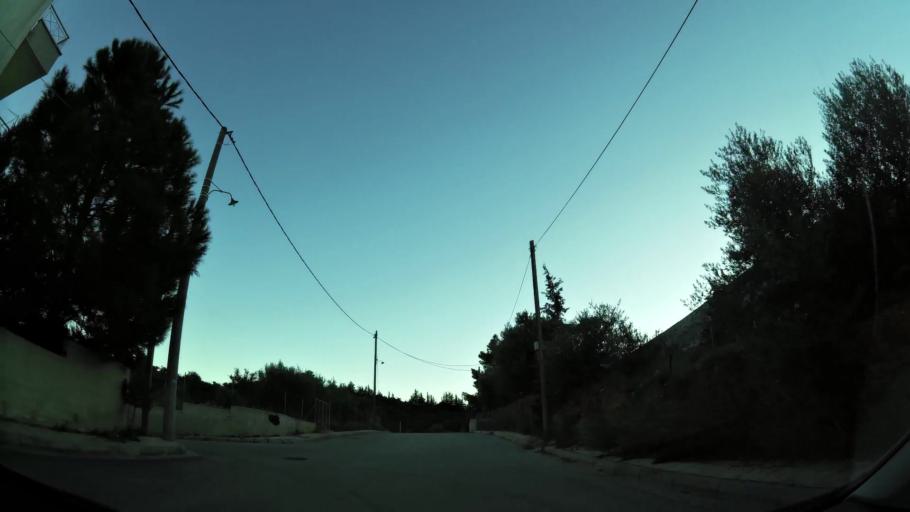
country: GR
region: Attica
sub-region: Nomarchia Anatolikis Attikis
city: Paiania
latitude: 37.9548
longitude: 23.8440
